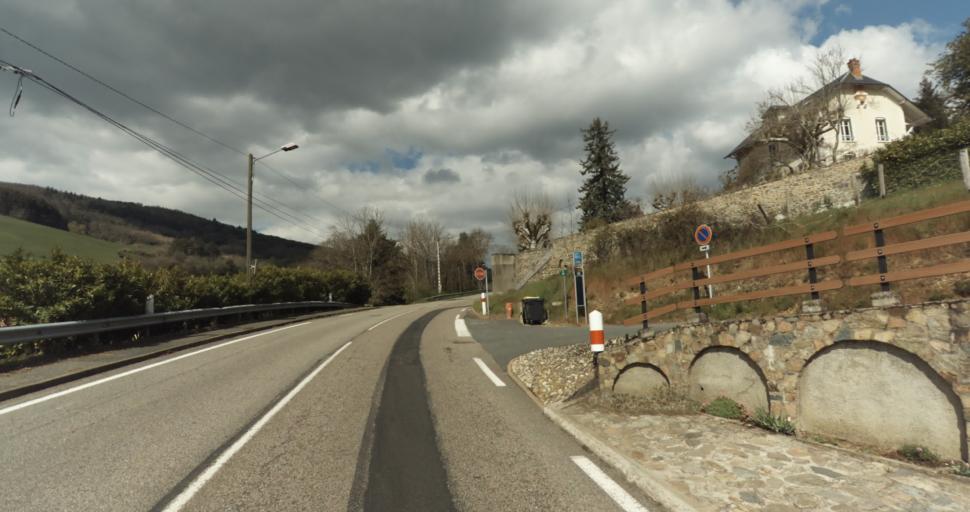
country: FR
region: Rhone-Alpes
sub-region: Departement du Rhone
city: Tarare
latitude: 45.9137
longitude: 4.4220
